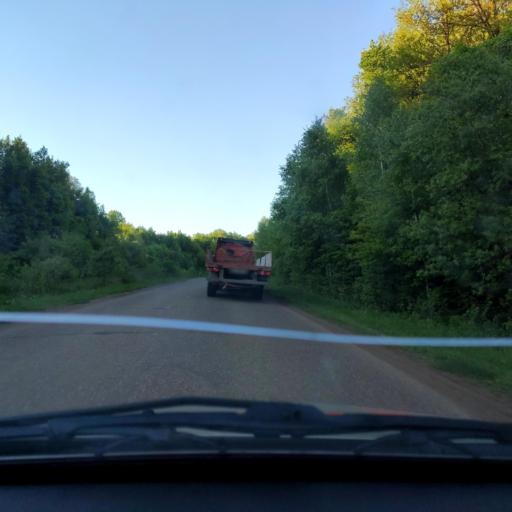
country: RU
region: Bashkortostan
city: Blagoveshchensk
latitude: 55.0328
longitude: 56.1148
